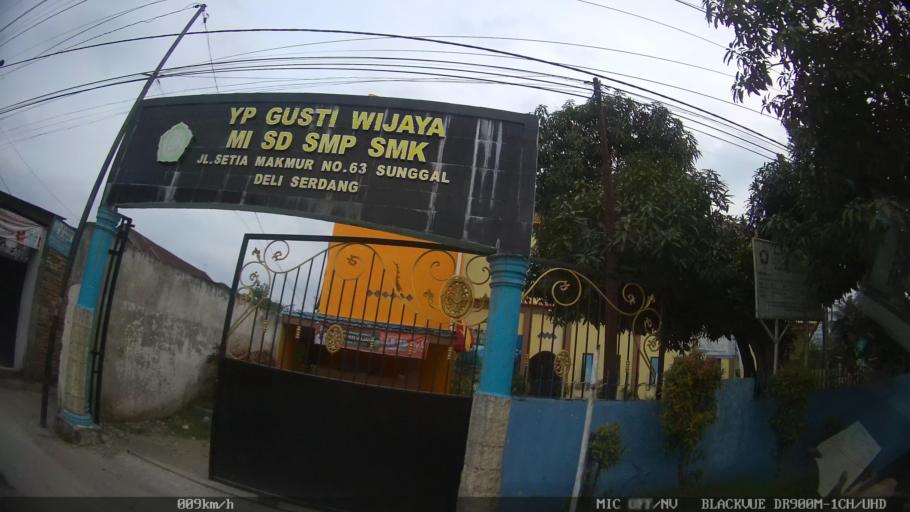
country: ID
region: North Sumatra
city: Sunggal
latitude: 3.5640
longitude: 98.5993
